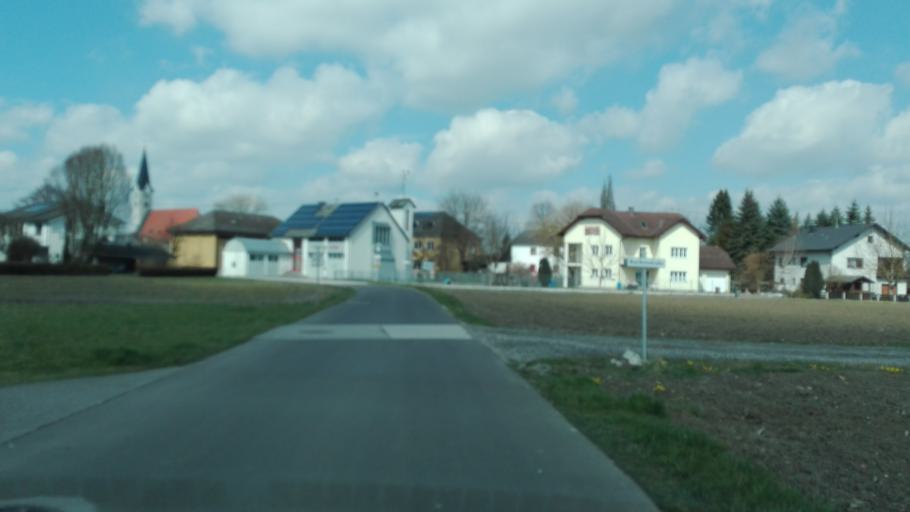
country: AT
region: Upper Austria
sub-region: Politischer Bezirk Urfahr-Umgebung
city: Goldworth
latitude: 48.3258
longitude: 14.1027
